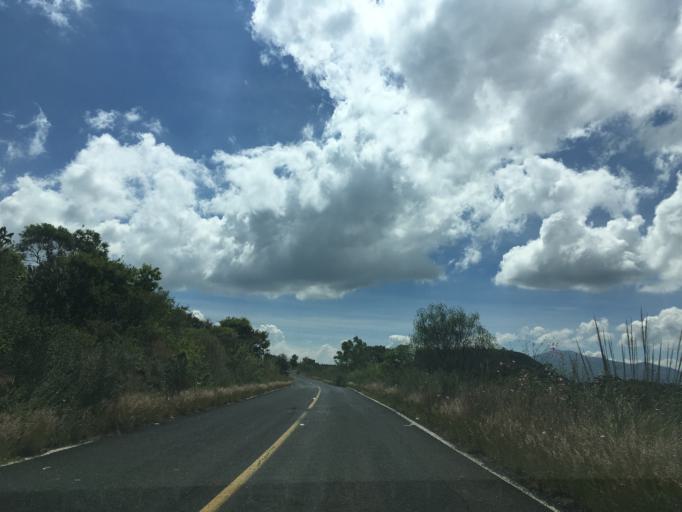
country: MX
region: Michoacan
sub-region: Morelia
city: Cuto de la Esperanza
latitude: 19.7497
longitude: -101.3704
